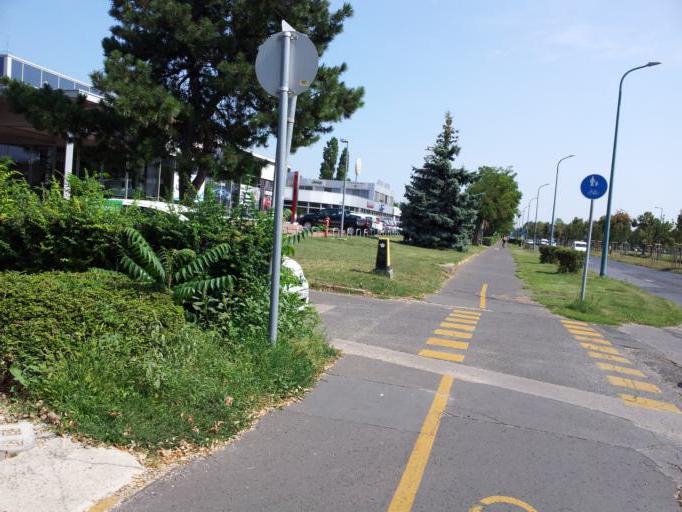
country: HU
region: Budapest
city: Budapest XIV. keruelet
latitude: 47.5069
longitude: 19.1148
